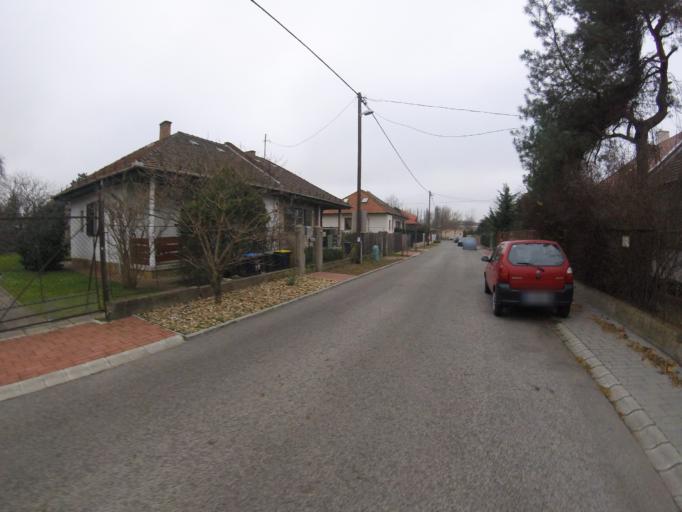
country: HU
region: Budapest
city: Budapest IV. keruelet
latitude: 47.5477
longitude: 19.0878
